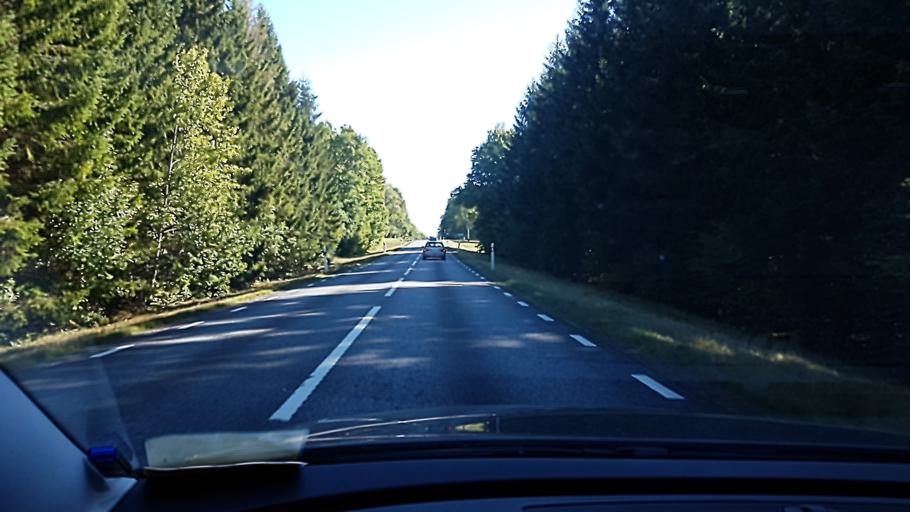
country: SE
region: Kalmar
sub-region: Emmaboda Kommun
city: Emmaboda
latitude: 56.7327
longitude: 15.4309
